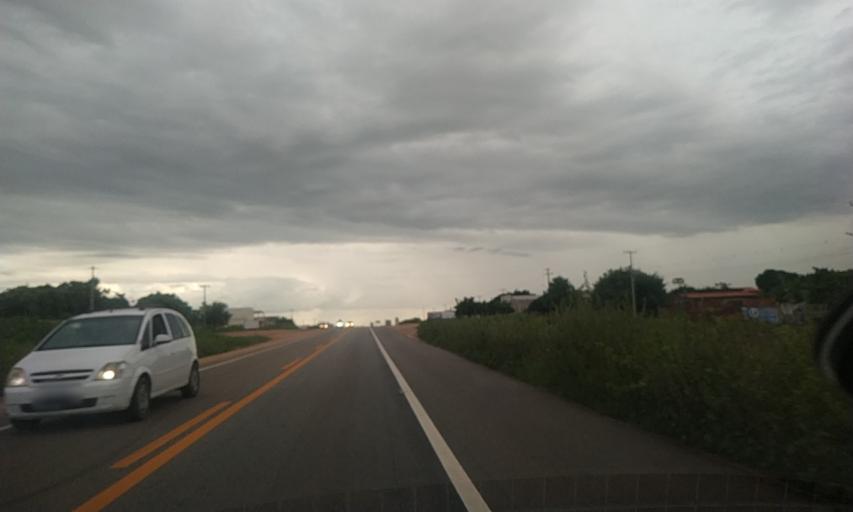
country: BR
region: Rio Grande do Norte
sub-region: Mossoro
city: Mossoro
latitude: -5.1883
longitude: -37.3055
